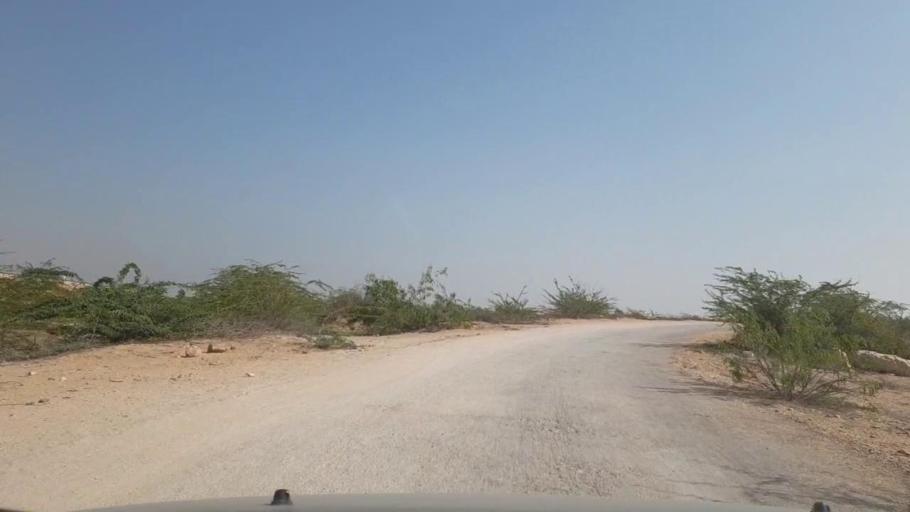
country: PK
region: Sindh
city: Thatta
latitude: 24.9826
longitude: 67.9908
